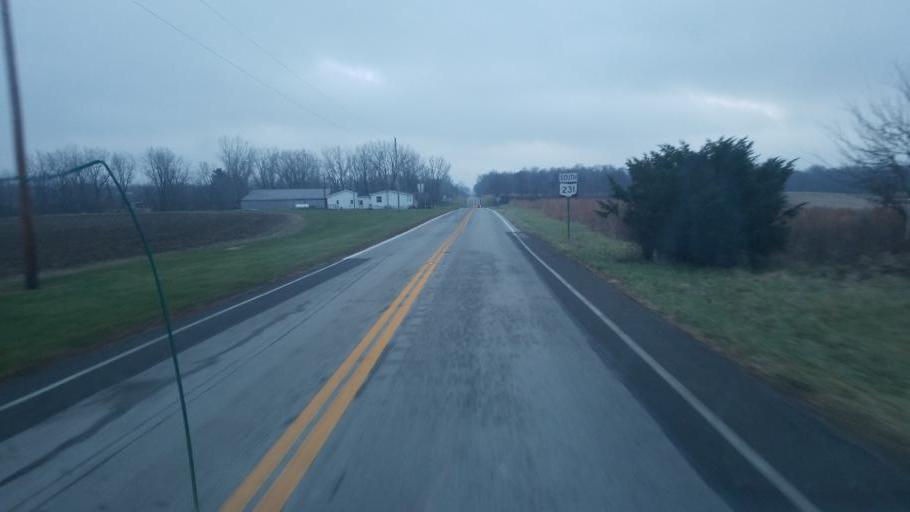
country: US
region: Ohio
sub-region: Seneca County
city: Tiffin
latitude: 40.9493
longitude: -83.1316
